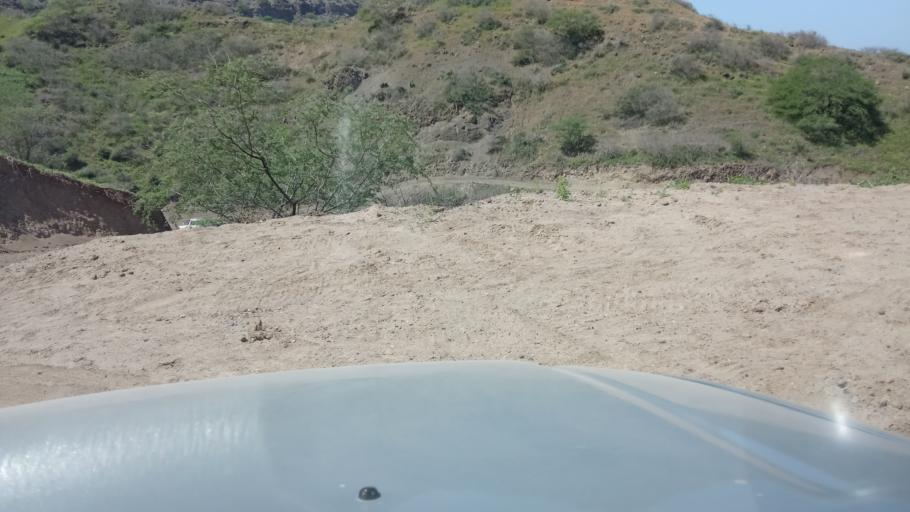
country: CV
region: Santa Catarina
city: Assomada
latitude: 15.1132
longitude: -23.7279
